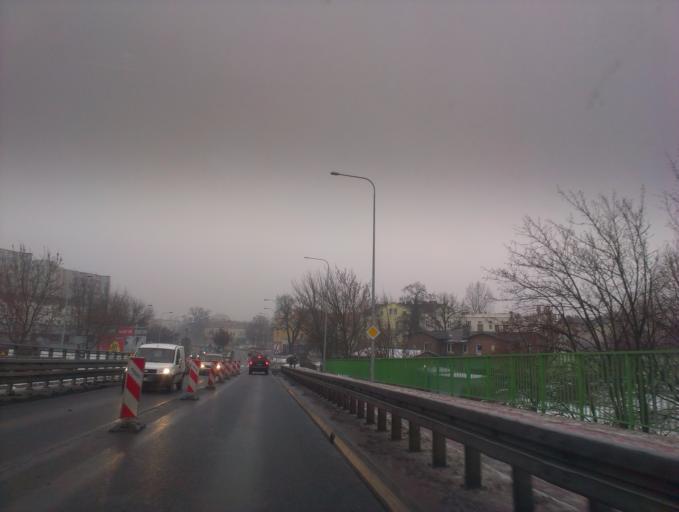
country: PL
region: Greater Poland Voivodeship
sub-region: Powiat pilski
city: Pila
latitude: 53.1442
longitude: 16.7399
